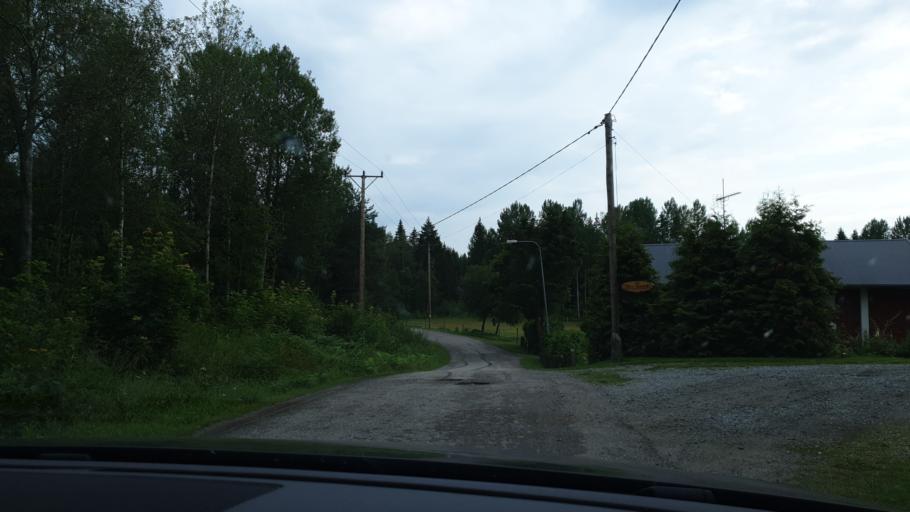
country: SE
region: Gaevleborg
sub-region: Hudiksvalls Kommun
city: Iggesund
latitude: 61.5387
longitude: 17.0094
